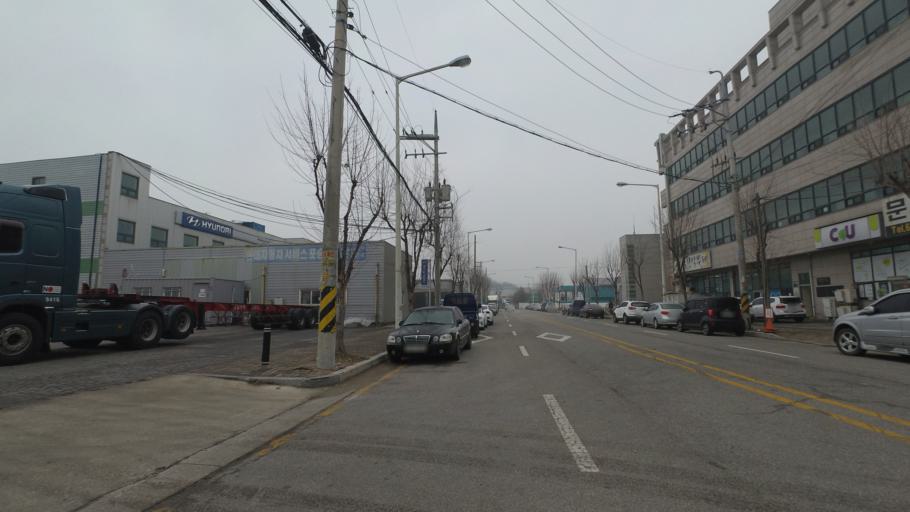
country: KR
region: Chungcheongnam-do
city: Tangjin
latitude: 36.9749
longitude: 126.8436
